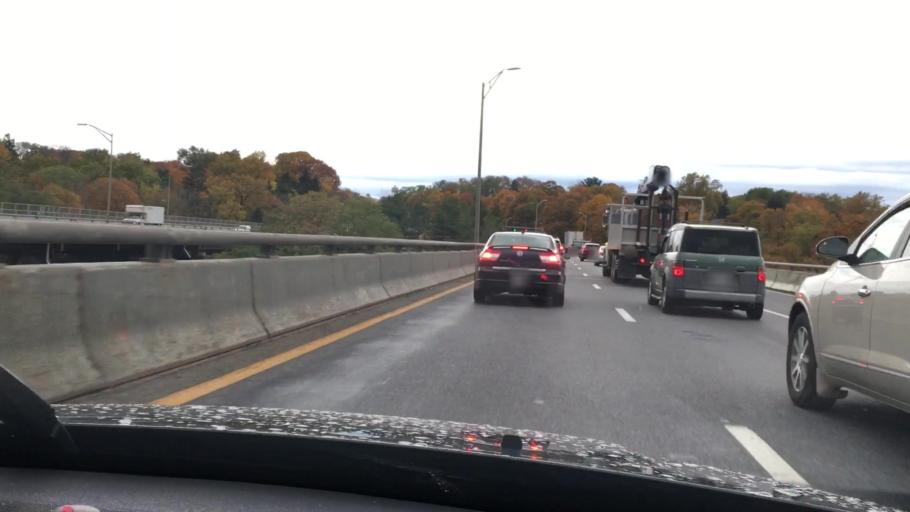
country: US
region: New York
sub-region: Orange County
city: Balmville
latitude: 41.5210
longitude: -74.0072
